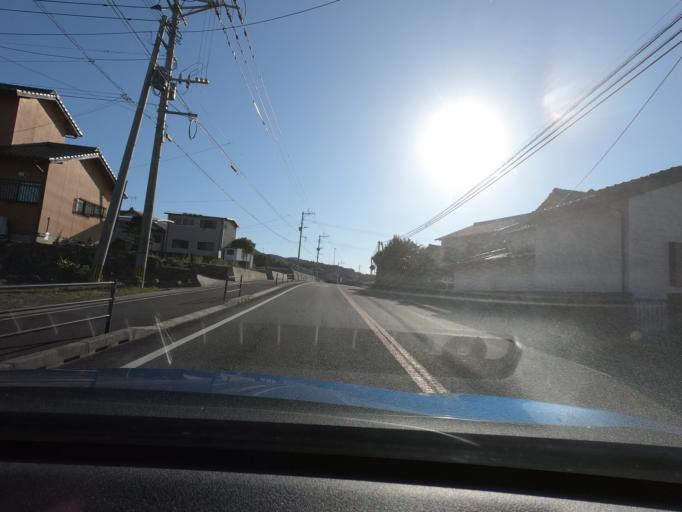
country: JP
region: Kumamoto
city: Minamata
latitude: 32.1744
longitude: 130.3827
